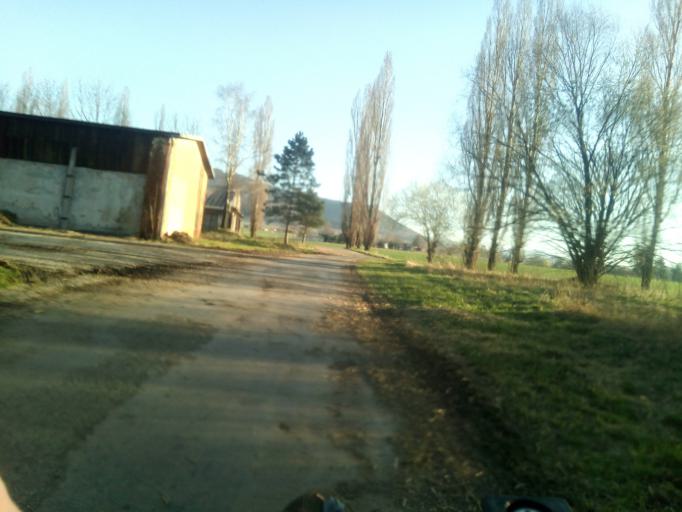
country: CZ
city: Dobratice
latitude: 49.6631
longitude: 18.4845
